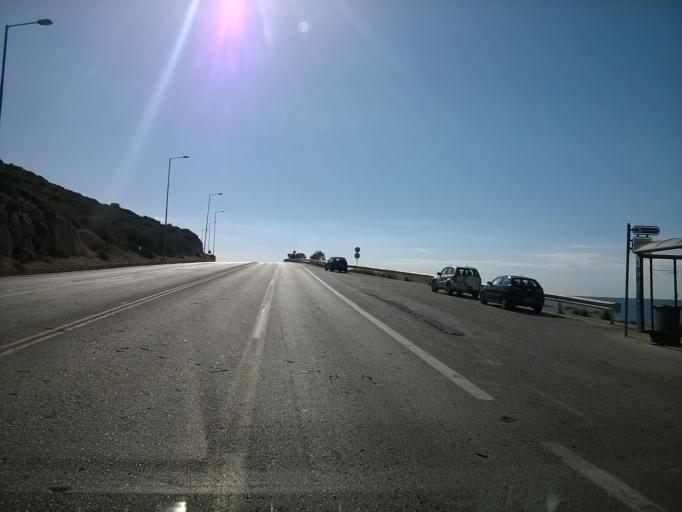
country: GR
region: Attica
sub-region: Nomarchia Anatolikis Attikis
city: Saronida
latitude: 37.7730
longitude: 23.9019
